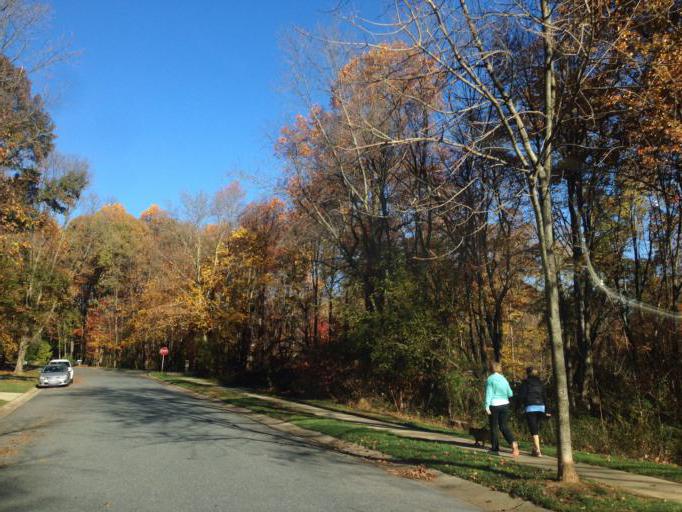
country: US
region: Maryland
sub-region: Howard County
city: Riverside
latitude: 39.1925
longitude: -76.8741
